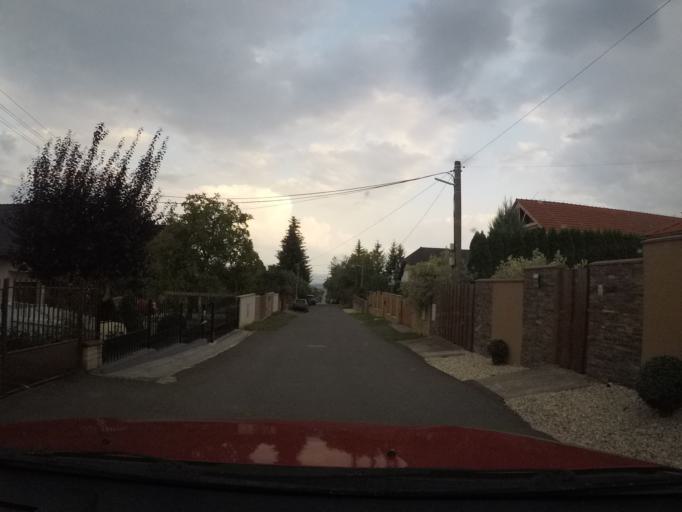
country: SK
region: Kosicky
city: Kosice
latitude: 48.6932
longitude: 21.2086
